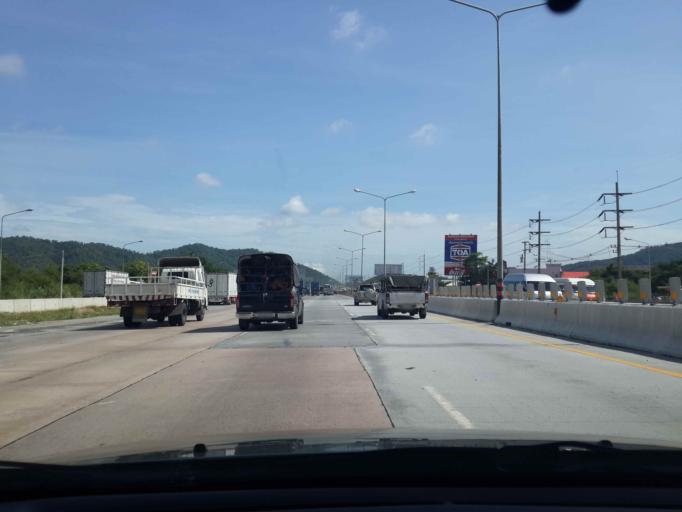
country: TH
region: Chon Buri
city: Si Racha
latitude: 13.2370
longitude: 100.9982
